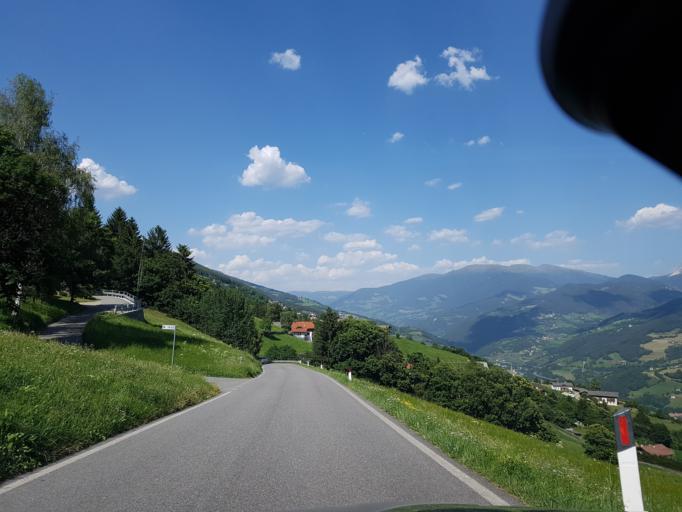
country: IT
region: Trentino-Alto Adige
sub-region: Bolzano
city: Villandro - Villanders
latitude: 46.6288
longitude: 11.5272
